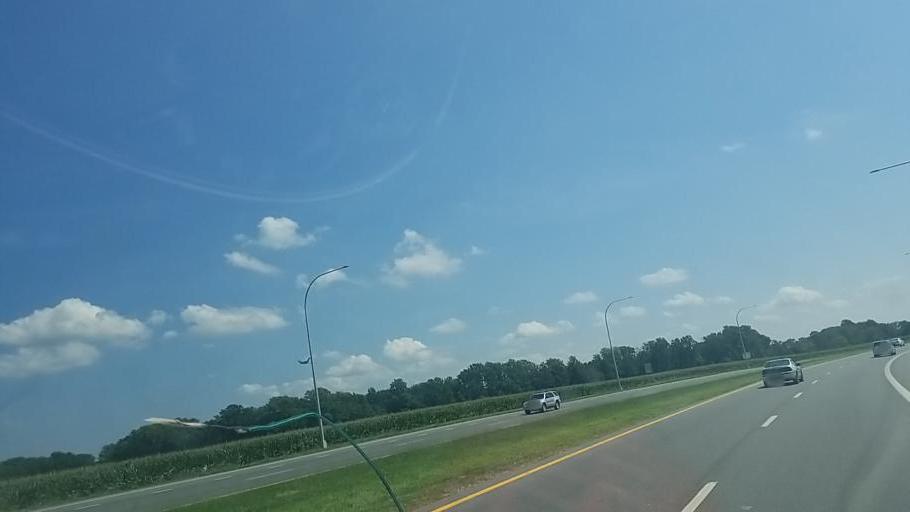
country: US
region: Delaware
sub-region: Kent County
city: Dover Base Housing
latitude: 39.1040
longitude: -75.4542
